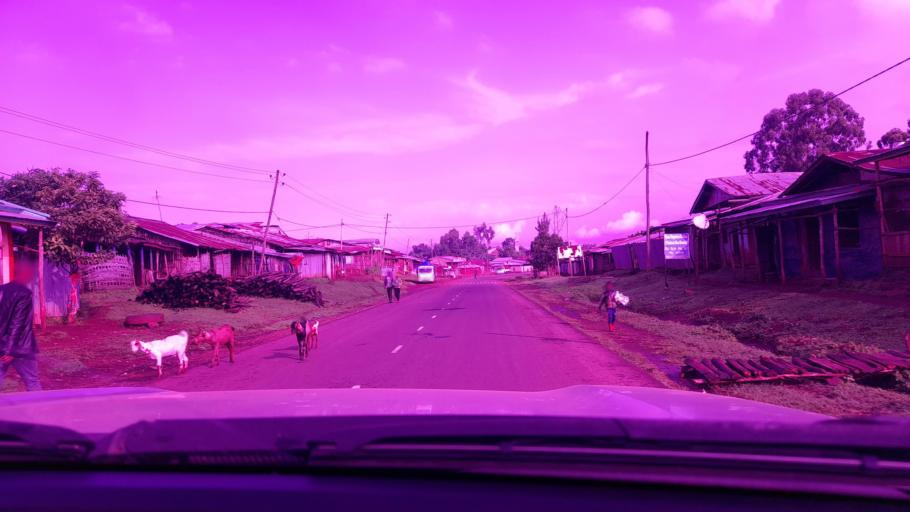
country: ET
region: Oromiya
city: Bedele
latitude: 8.1713
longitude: 36.4619
